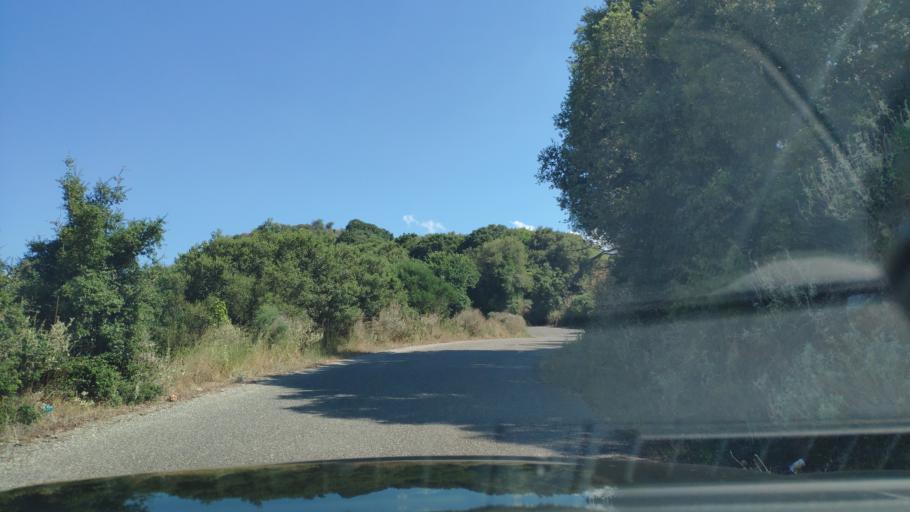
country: GR
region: West Greece
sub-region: Nomos Aitolias kai Akarnanias
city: Katouna
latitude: 38.8072
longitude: 21.1093
